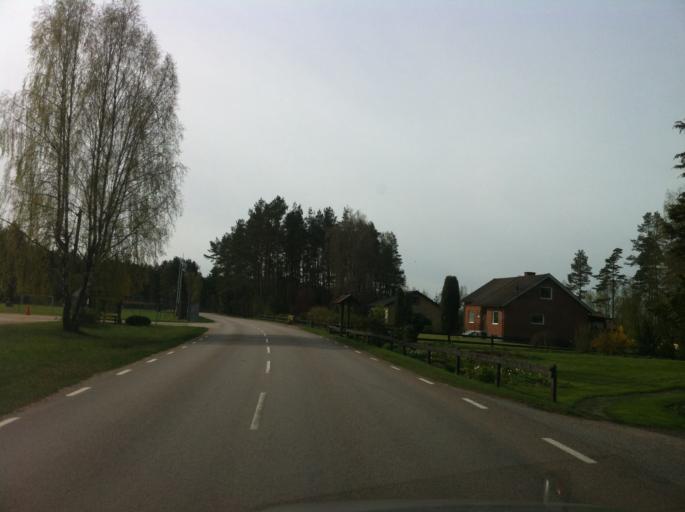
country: SE
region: Vaestra Goetaland
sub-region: Bollebygds Kommun
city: Bollebygd
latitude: 57.7119
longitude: 12.5815
